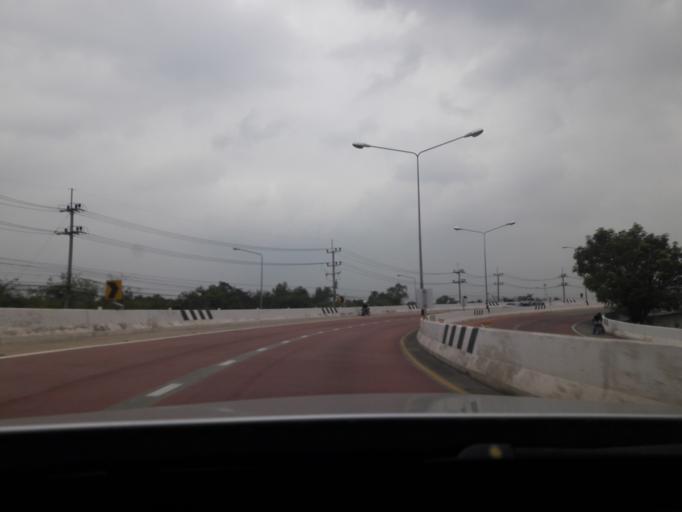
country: TH
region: Samut Songkhram
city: Samut Songkhram
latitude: 13.3989
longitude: 100.0090
